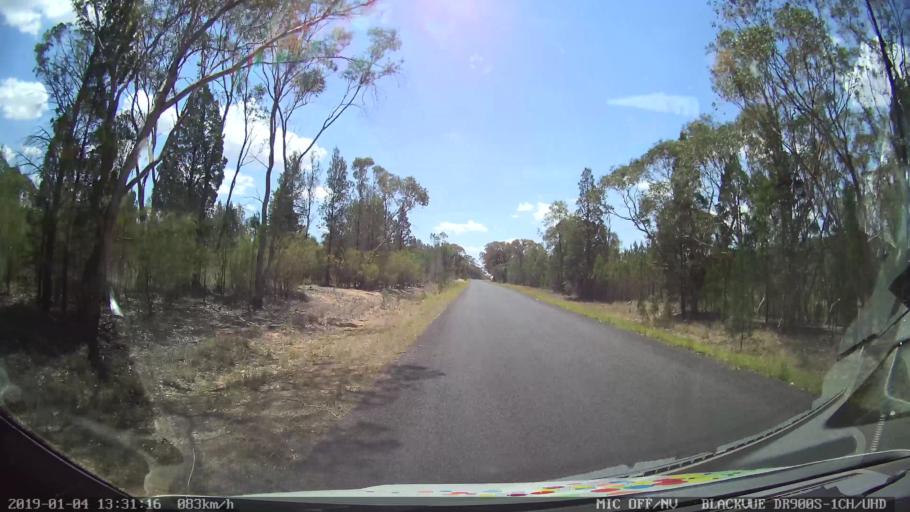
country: AU
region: New South Wales
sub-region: Parkes
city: Peak Hill
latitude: -32.6248
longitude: 148.5489
